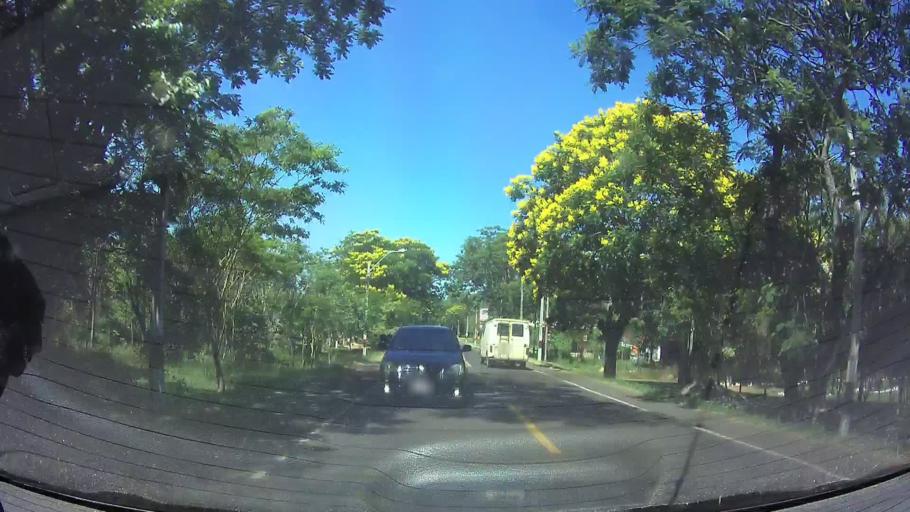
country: PY
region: Central
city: Aregua
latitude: -25.3250
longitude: -57.3945
